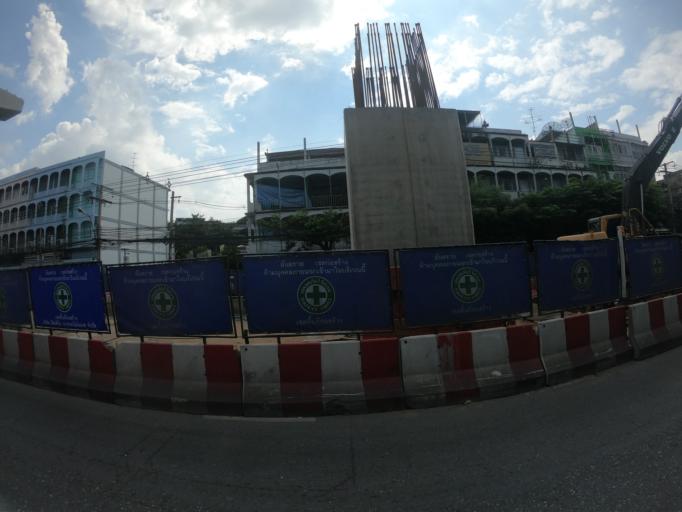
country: TH
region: Bangkok
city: Lat Phrao
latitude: 13.7942
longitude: 100.5947
